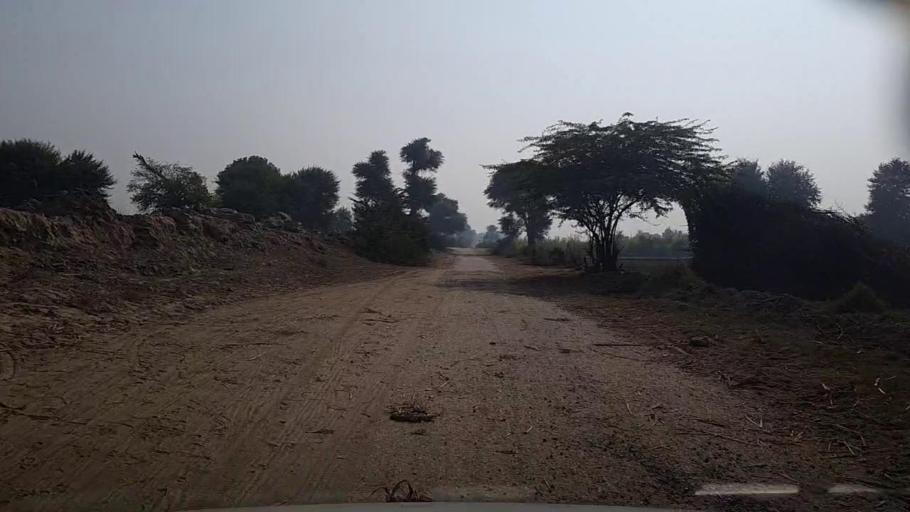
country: PK
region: Sindh
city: Setharja Old
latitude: 27.1367
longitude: 68.5108
